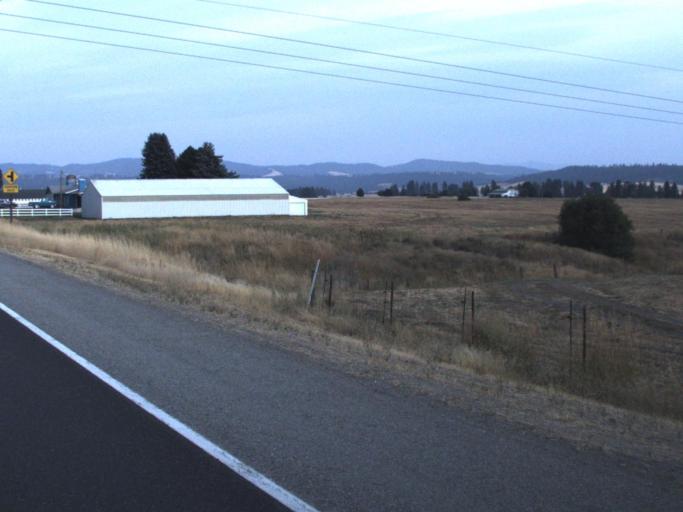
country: US
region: Washington
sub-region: Spokane County
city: Mead
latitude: 47.7873
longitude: -117.3313
